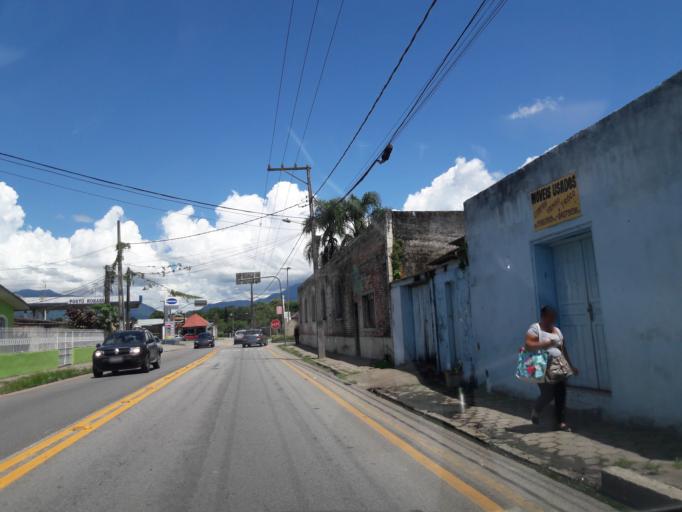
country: BR
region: Parana
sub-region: Antonina
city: Antonina
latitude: -25.4814
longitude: -48.8295
